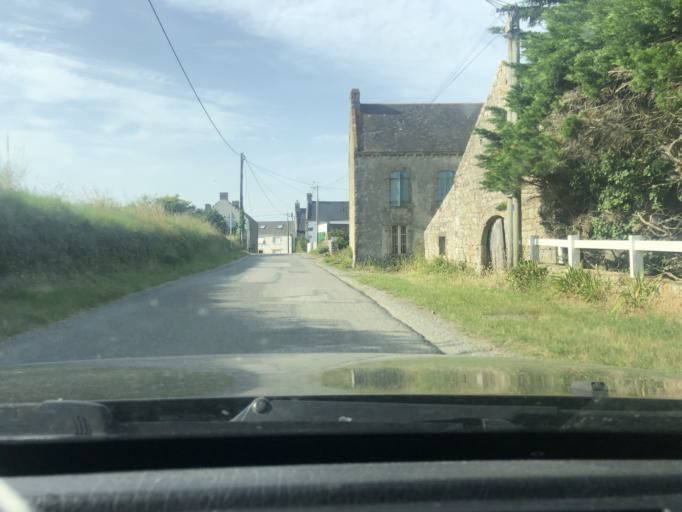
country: FR
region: Brittany
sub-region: Departement du Morbihan
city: Erdeven
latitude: 47.6259
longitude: -3.1806
